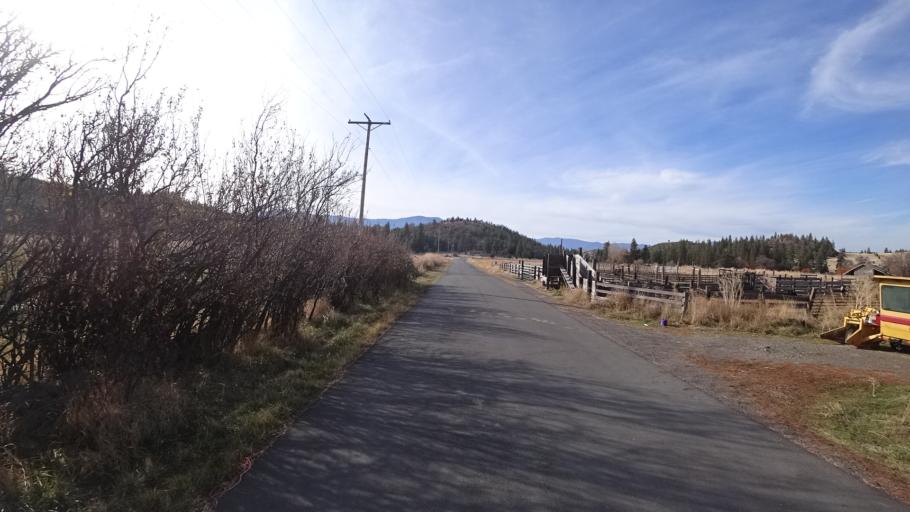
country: US
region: California
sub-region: Siskiyou County
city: Weed
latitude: 41.4651
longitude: -122.3977
